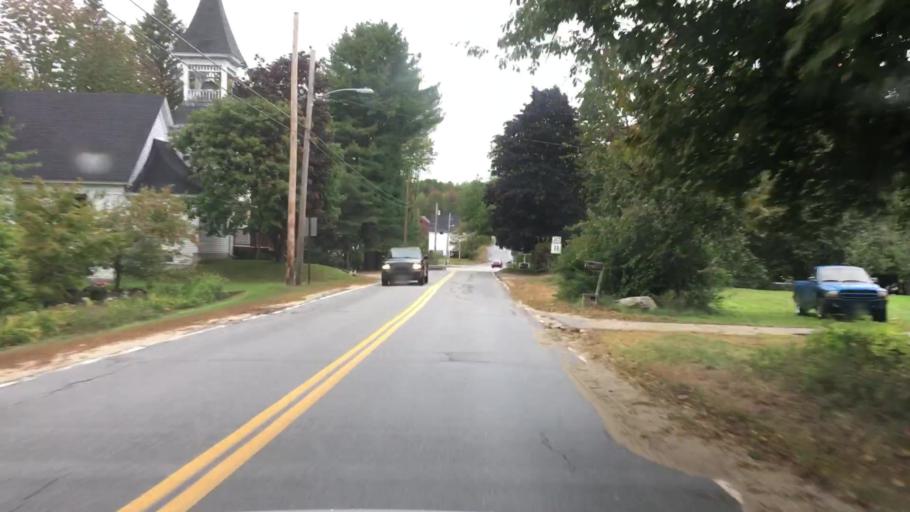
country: US
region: Maine
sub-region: Cumberland County
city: Raymond
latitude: 43.9848
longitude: -70.4752
